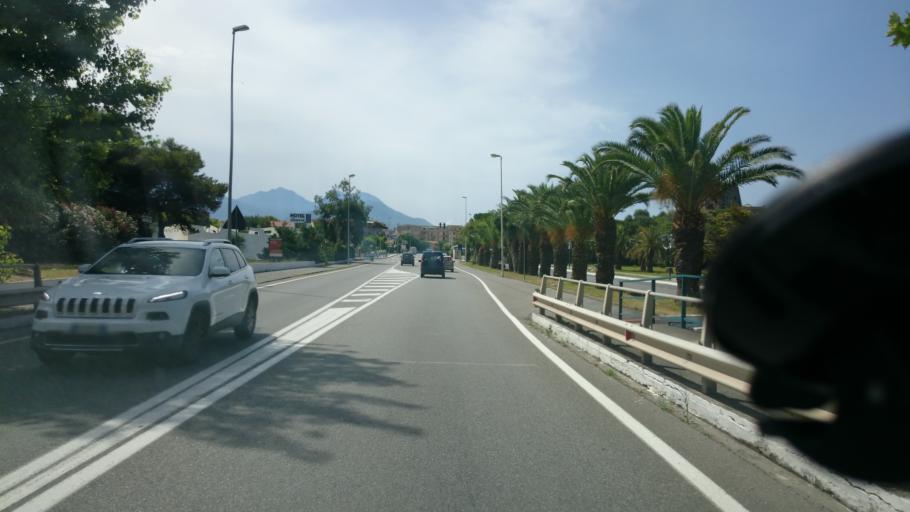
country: IT
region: Calabria
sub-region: Provincia di Cosenza
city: Scalea
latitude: 39.8154
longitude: 15.7880
